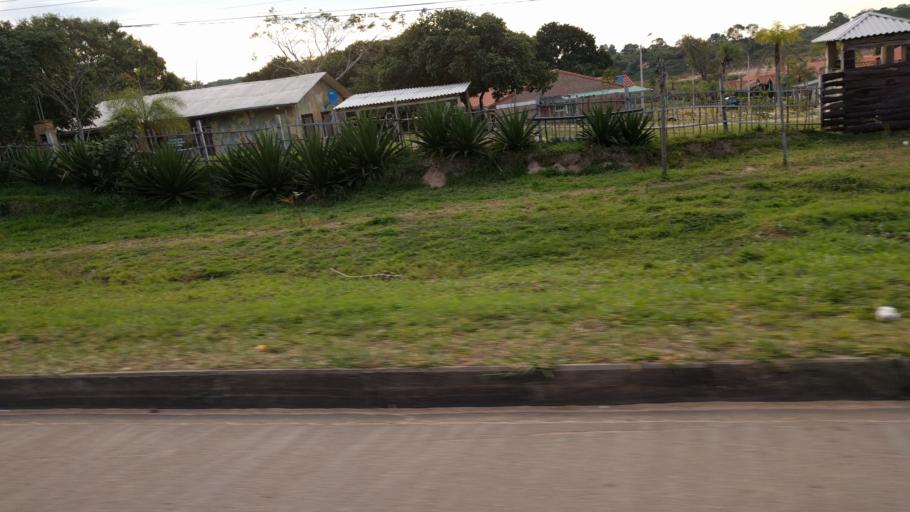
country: BO
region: Santa Cruz
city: Buena Vista
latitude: -17.4544
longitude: -63.6560
